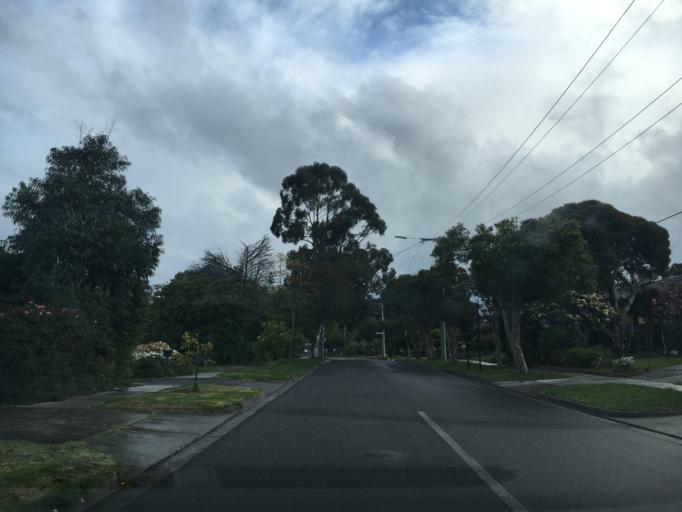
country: AU
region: Victoria
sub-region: Whitehorse
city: Vermont South
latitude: -37.8815
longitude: 145.1791
